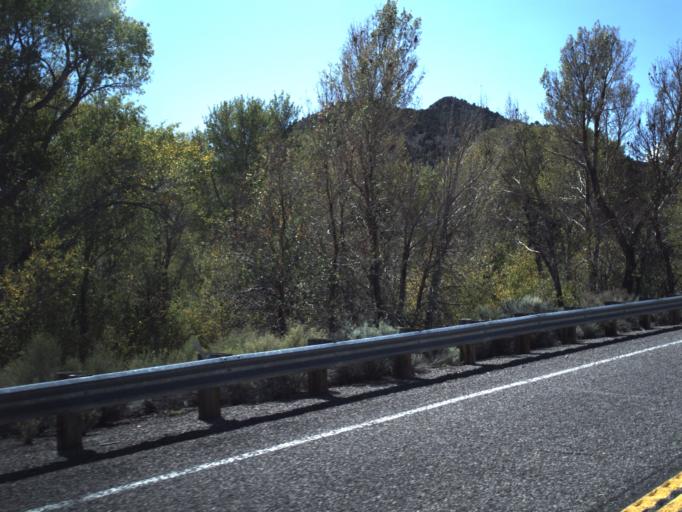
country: US
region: Utah
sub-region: Piute County
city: Junction
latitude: 38.2583
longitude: -112.2660
